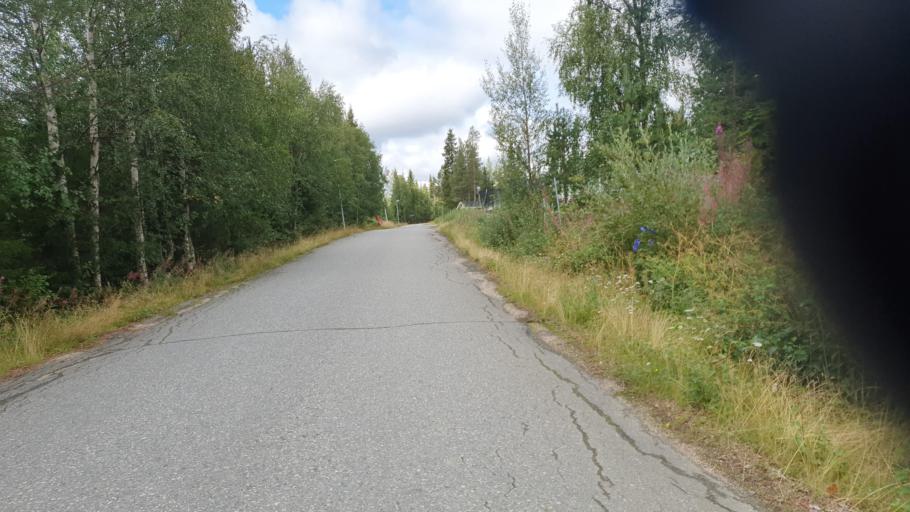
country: FI
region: Lapland
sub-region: Tunturi-Lappi
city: Kolari
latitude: 67.6188
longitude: 24.1506
